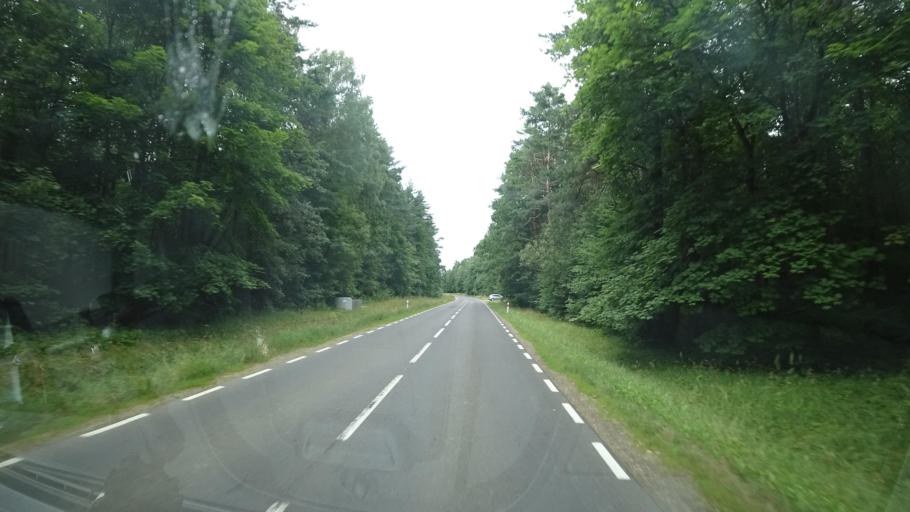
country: PL
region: Warmian-Masurian Voivodeship
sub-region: Powiat goldapski
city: Goldap
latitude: 54.3259
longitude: 22.2980
